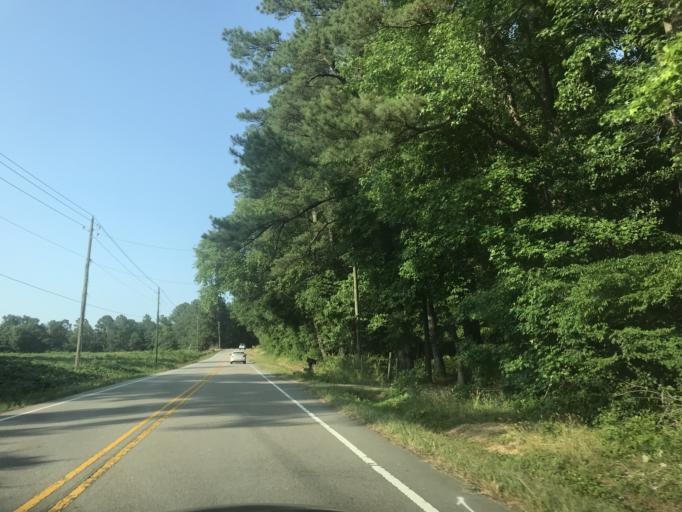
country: US
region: North Carolina
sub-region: Wake County
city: Knightdale
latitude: 35.8583
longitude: -78.4953
